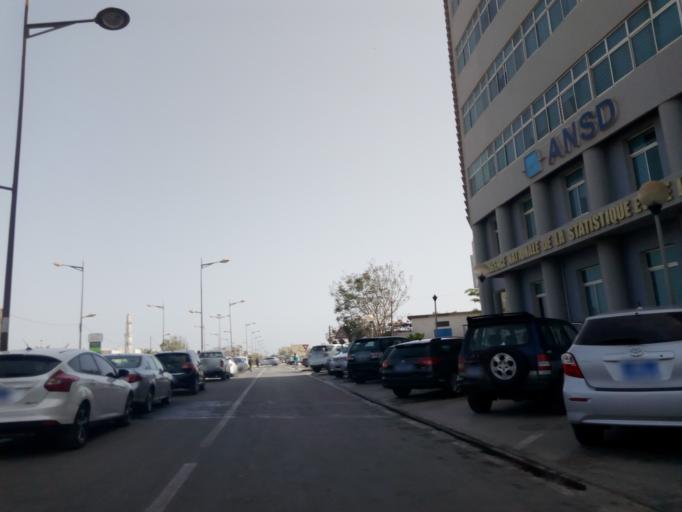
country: SN
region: Dakar
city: Dakar
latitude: 14.6989
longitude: -17.4497
